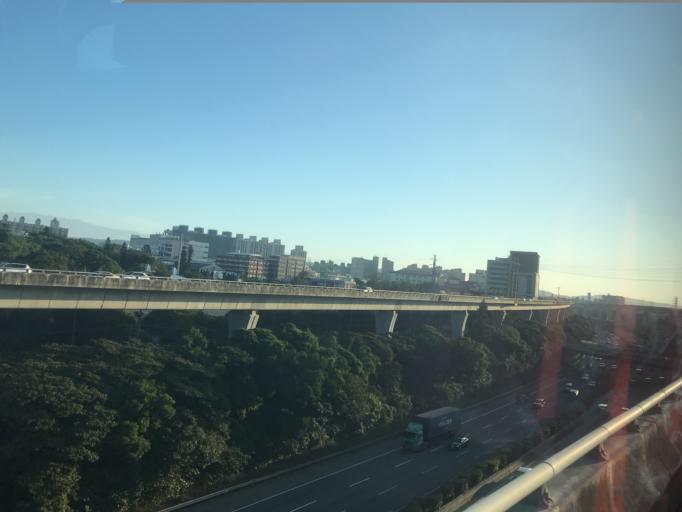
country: TW
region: Taiwan
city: Daxi
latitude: 24.9293
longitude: 121.1759
